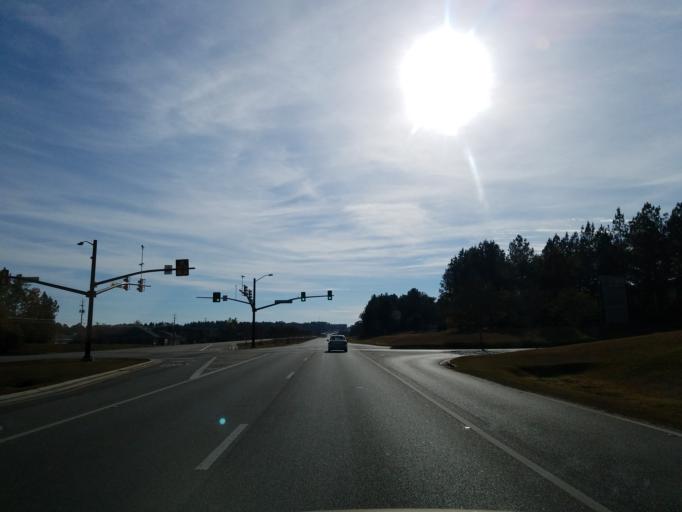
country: US
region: Mississippi
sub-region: Forrest County
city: Hattiesburg
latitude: 31.2821
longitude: -89.3252
